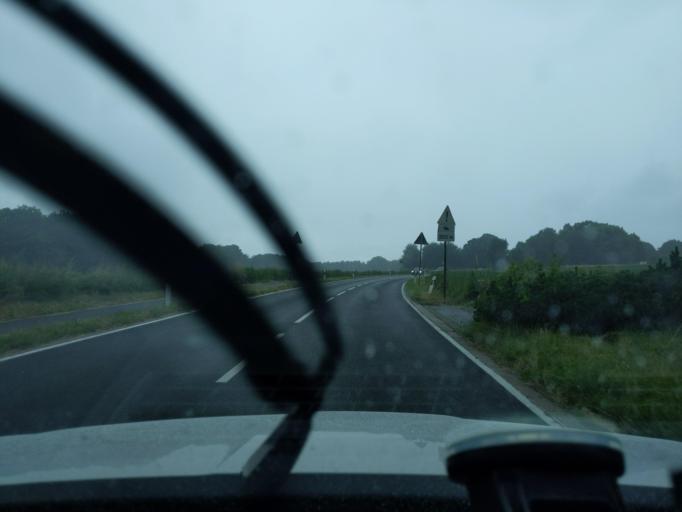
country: DE
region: North Rhine-Westphalia
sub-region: Regierungsbezirk Dusseldorf
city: Ratingen
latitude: 51.2706
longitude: 6.8691
